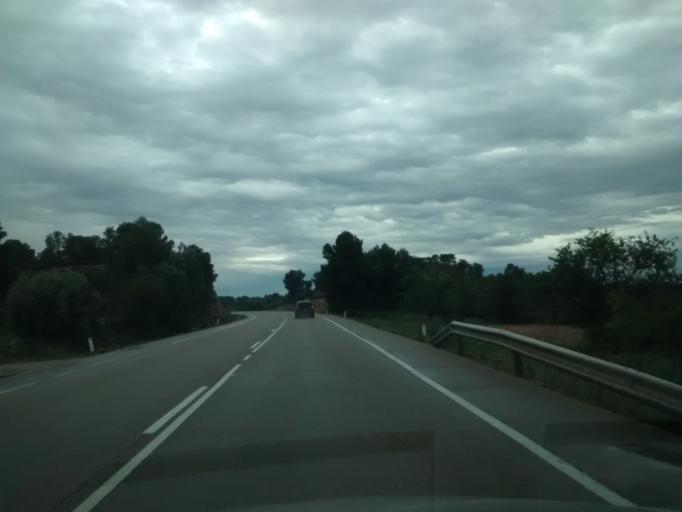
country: ES
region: Aragon
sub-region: Provincia de Zaragoza
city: Maella
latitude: 41.1518
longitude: 0.1019
